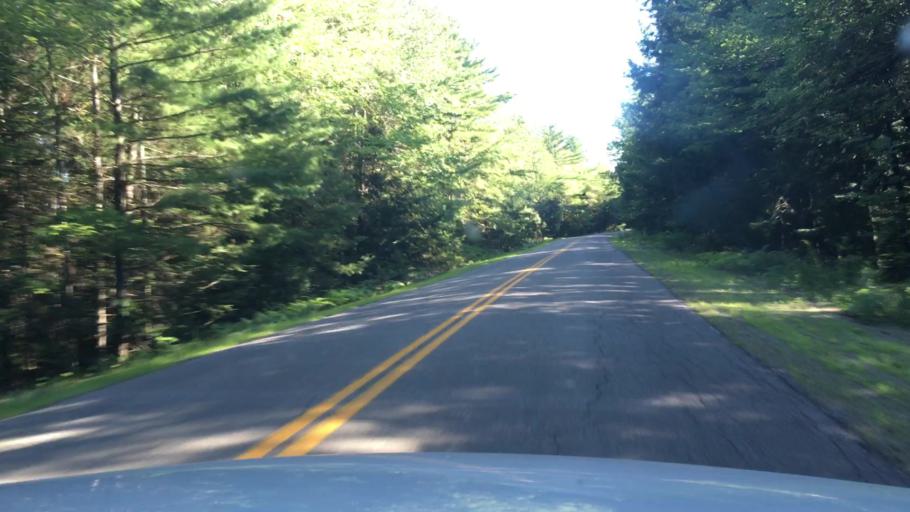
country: US
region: Maine
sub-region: Penobscot County
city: Enfield
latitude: 45.2222
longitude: -68.5803
